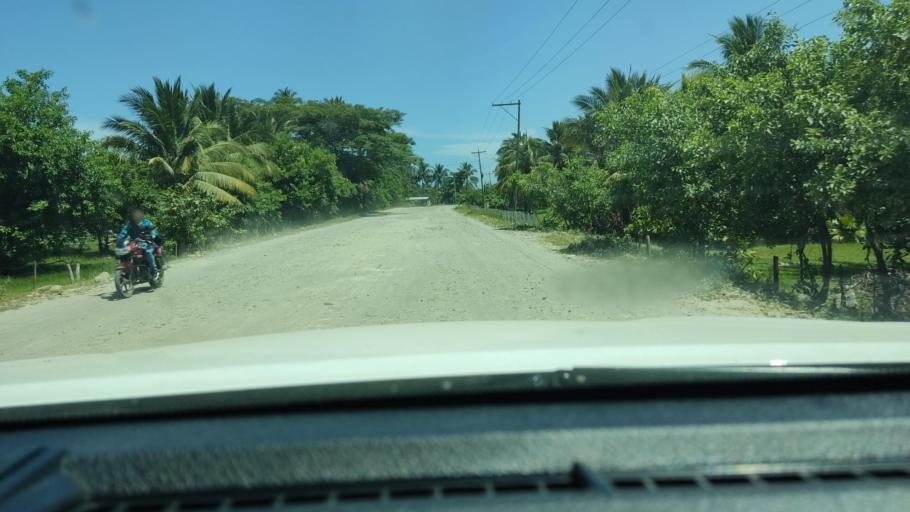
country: SV
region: Ahuachapan
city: San Francisco Menendez
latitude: 13.7648
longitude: -90.1159
